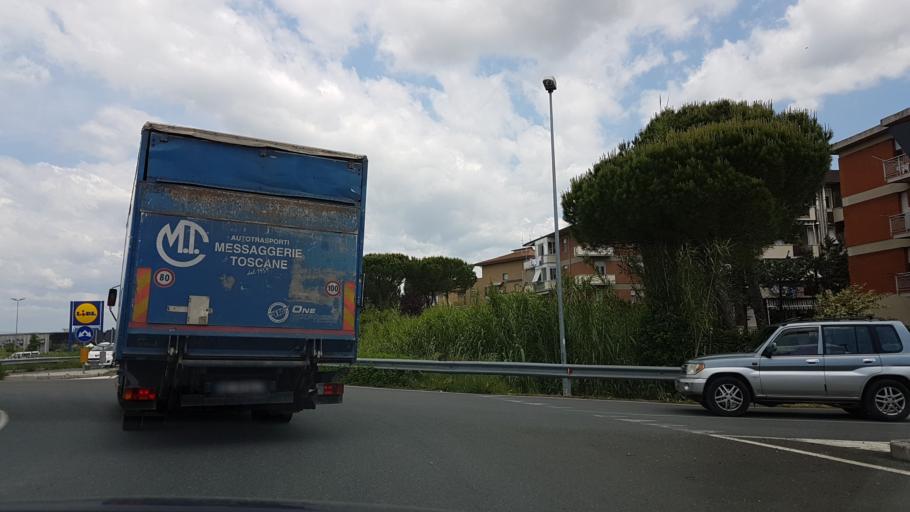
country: IT
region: Tuscany
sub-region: Provincia di Livorno
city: Collesalvetti
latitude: 43.5956
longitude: 10.4727
